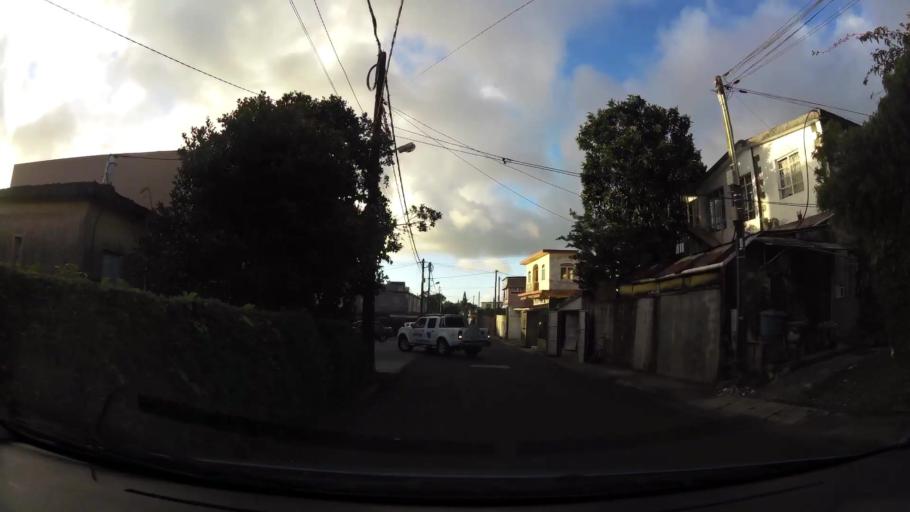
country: MU
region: Plaines Wilhems
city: Curepipe
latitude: -20.3133
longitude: 57.5297
